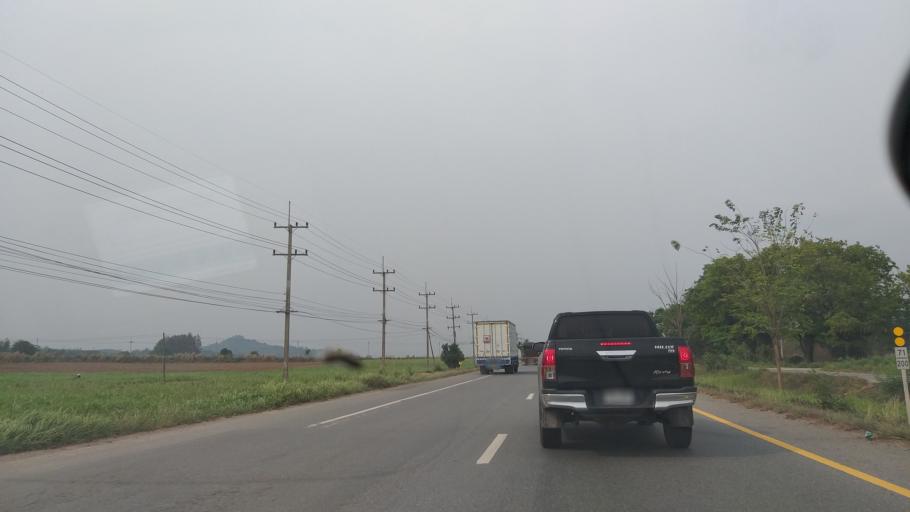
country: TH
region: Chon Buri
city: Ban Bueng
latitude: 13.2480
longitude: 101.2448
